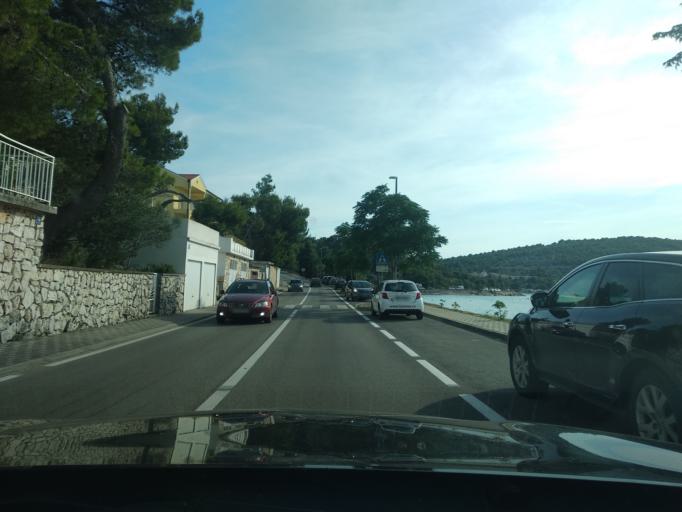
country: HR
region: Sibensko-Kniniska
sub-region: Grad Sibenik
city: Tisno
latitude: 43.7975
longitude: 15.6348
